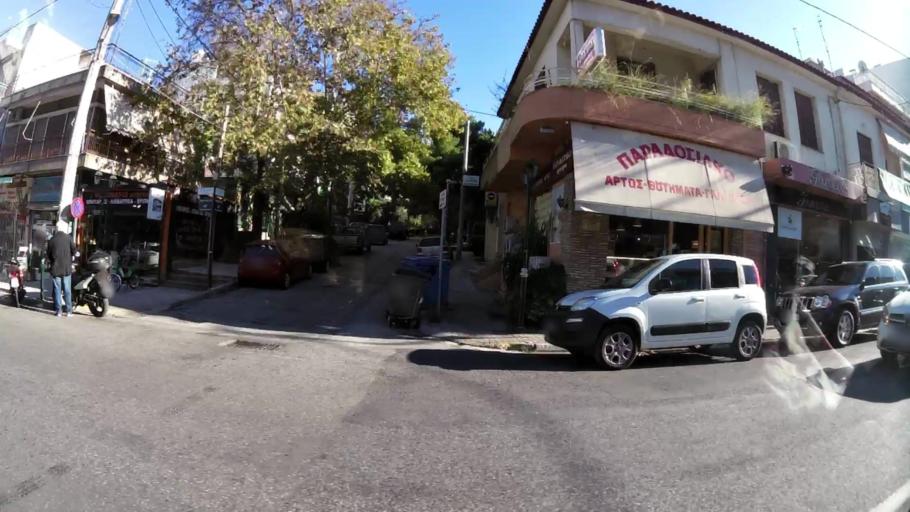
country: GR
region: Attica
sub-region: Nomarchia Athinas
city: Nea Erythraia
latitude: 38.0908
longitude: 23.8205
